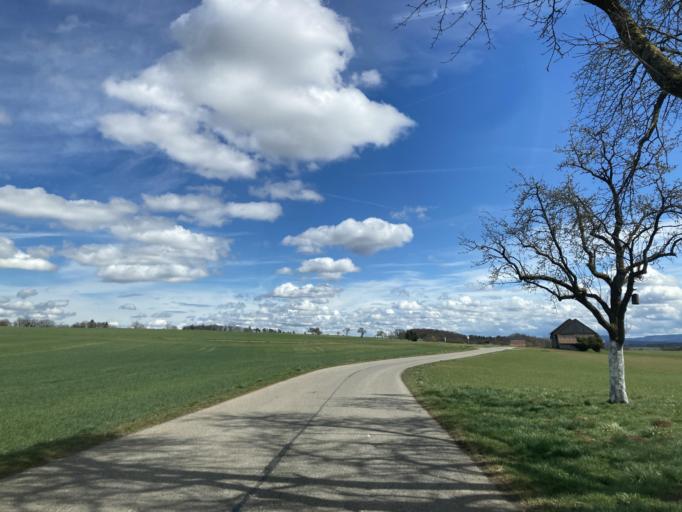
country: DE
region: Baden-Wuerttemberg
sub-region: Regierungsbezirk Stuttgart
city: Bondorf
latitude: 48.4571
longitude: 8.8399
